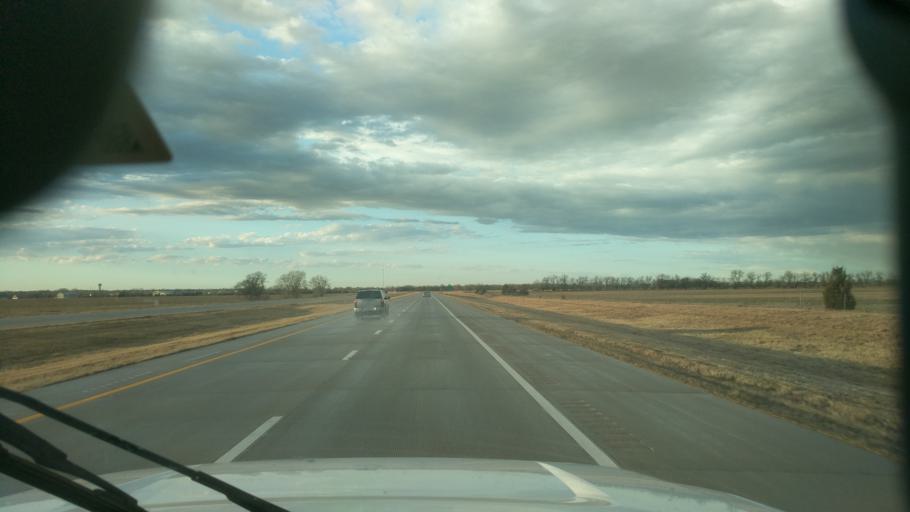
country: US
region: Kansas
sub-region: Harvey County
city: Hesston
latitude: 38.1256
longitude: -97.3973
